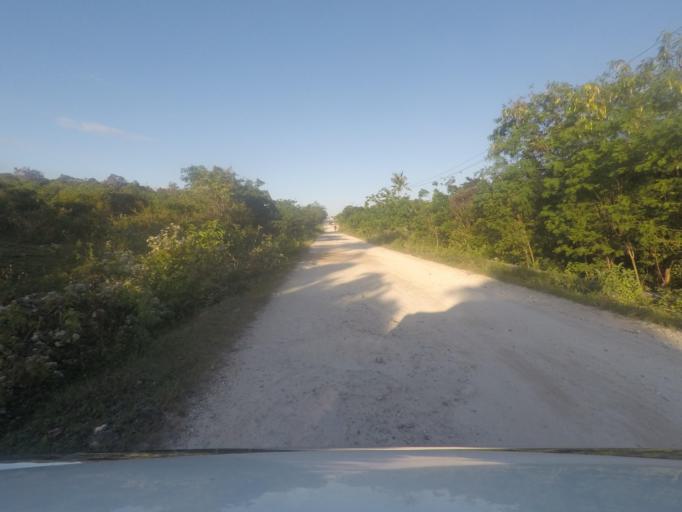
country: TL
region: Lautem
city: Lospalos
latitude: -8.3990
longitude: 127.2001
